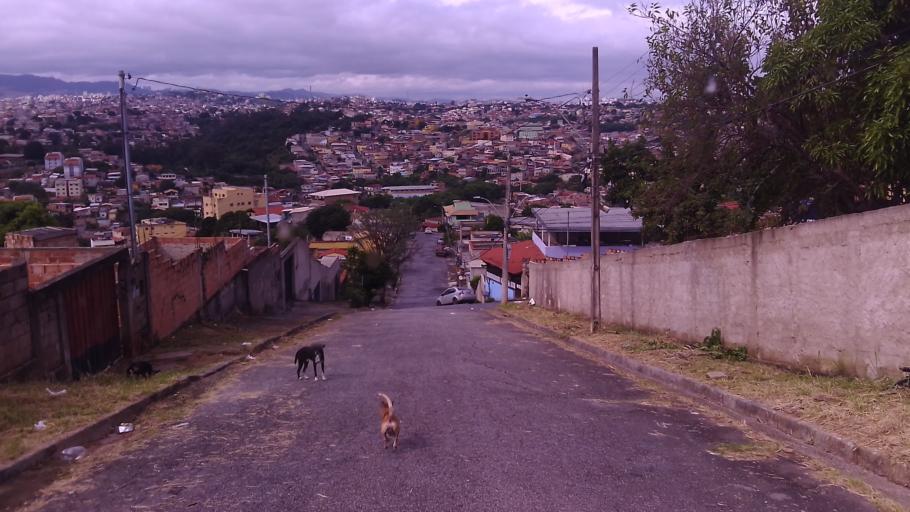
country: BR
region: Minas Gerais
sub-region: Santa Luzia
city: Santa Luzia
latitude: -19.8382
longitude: -43.8992
